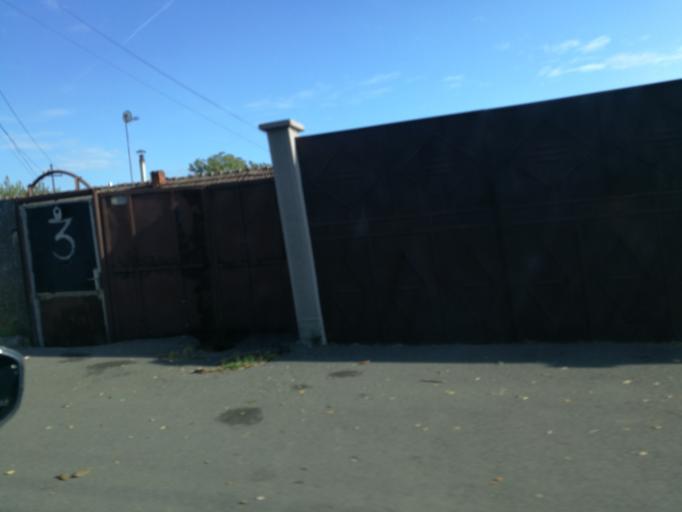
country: RO
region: Bihor
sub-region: Comuna Biharea
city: Oradea
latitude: 47.0373
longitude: 21.9413
